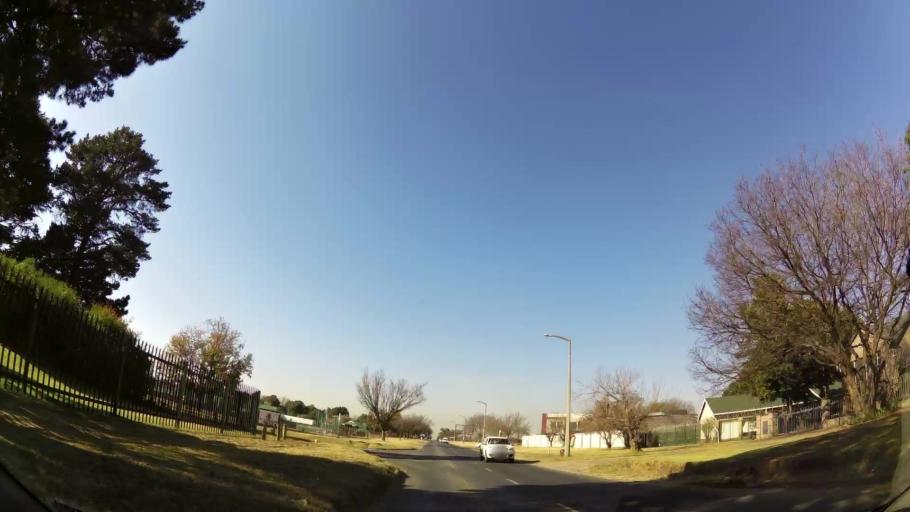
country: ZA
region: Gauteng
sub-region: Ekurhuleni Metropolitan Municipality
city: Benoni
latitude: -26.1495
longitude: 28.3154
